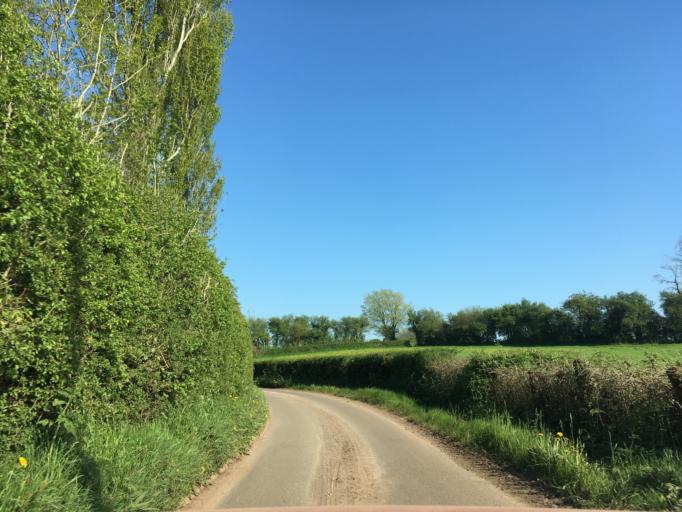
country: GB
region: Wales
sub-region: Monmouthshire
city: Caldicot
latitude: 51.6381
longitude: -2.7359
